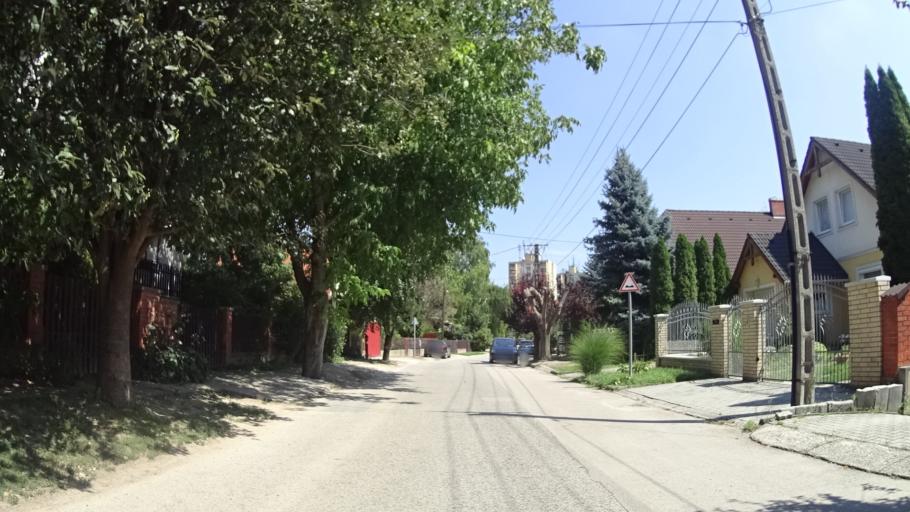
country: HU
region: Fejer
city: Szekesfehervar
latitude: 47.1944
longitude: 18.4575
